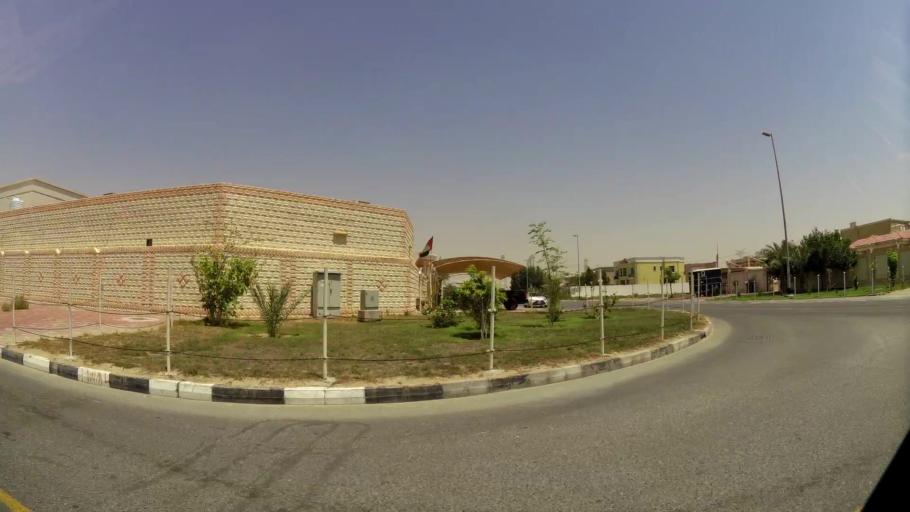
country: AE
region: Dubai
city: Dubai
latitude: 25.0857
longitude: 55.2088
